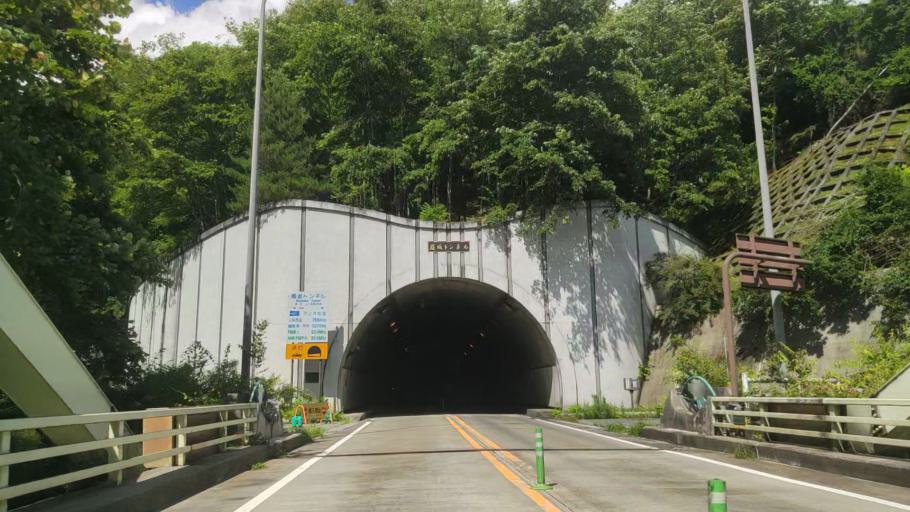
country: JP
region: Yamanashi
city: Enzan
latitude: 35.8645
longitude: 138.7659
